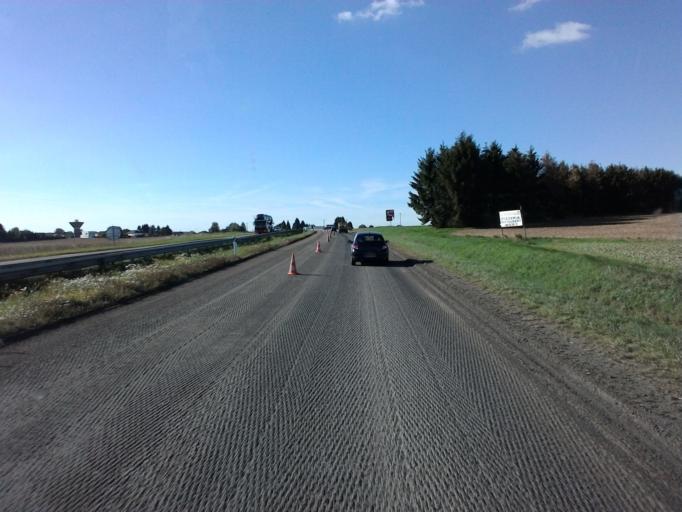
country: FR
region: Lorraine
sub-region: Departement de Meurthe-et-Moselle
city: Haucourt-Moulaine
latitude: 49.4993
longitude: 5.8022
